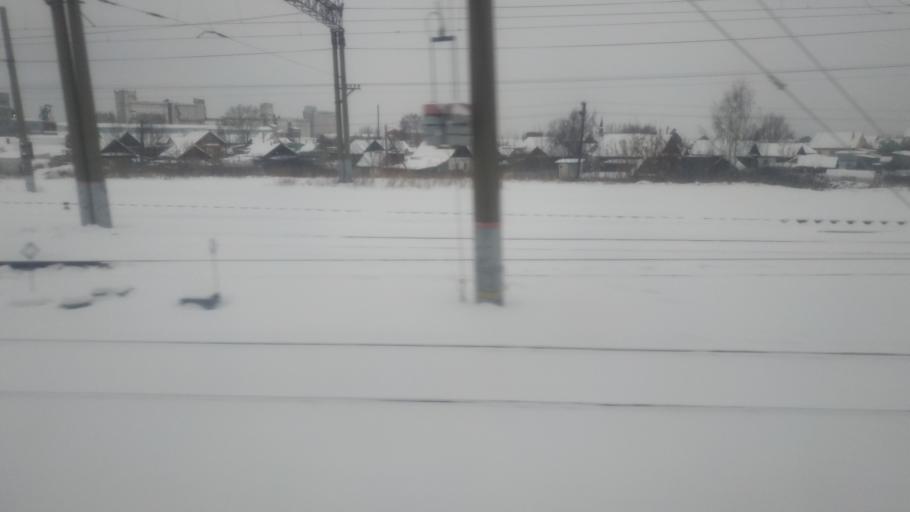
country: RU
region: Bashkortostan
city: Yanaul
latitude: 56.2753
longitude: 54.9395
